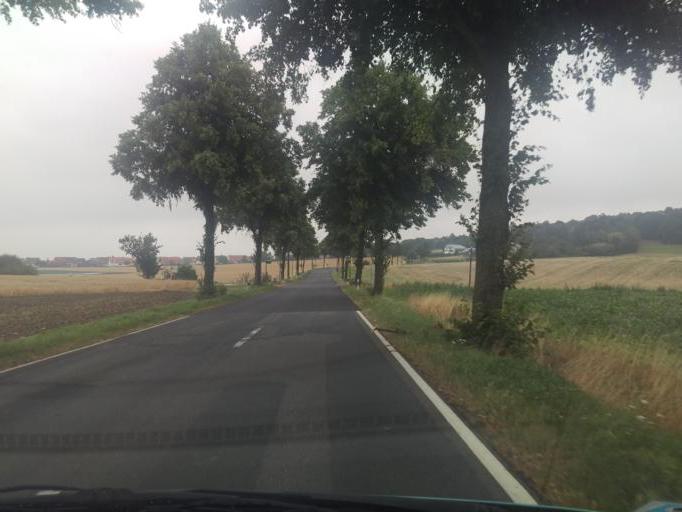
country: DE
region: Lower Saxony
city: Schellerten
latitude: 52.1431
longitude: 10.0761
